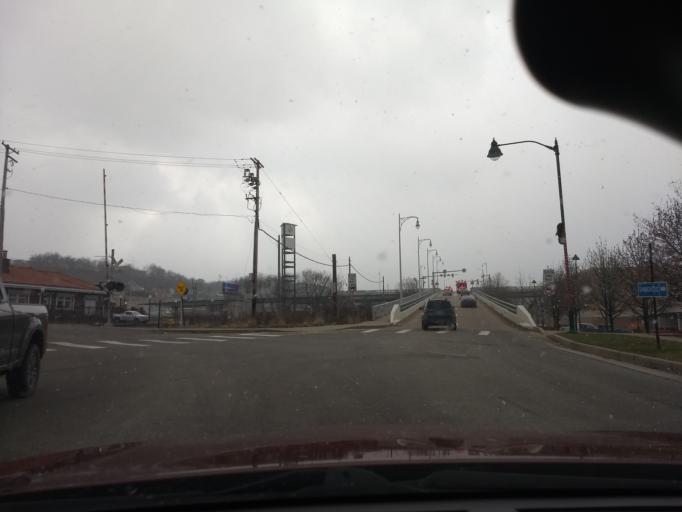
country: US
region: Pennsylvania
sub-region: Allegheny County
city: Homestead
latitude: 40.4088
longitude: -79.9124
